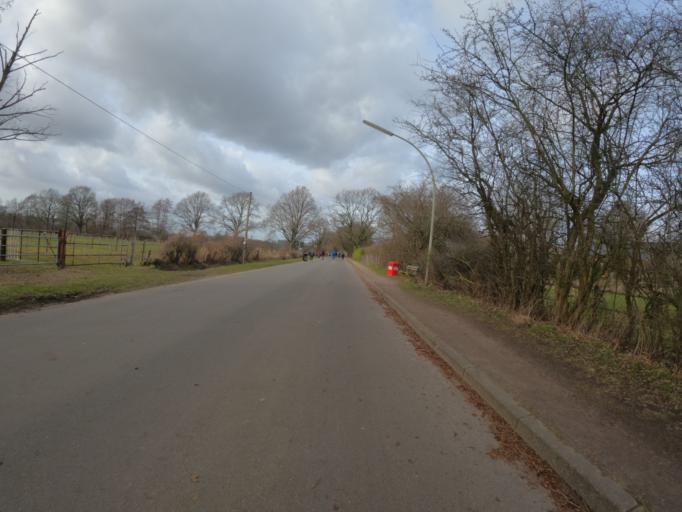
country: DE
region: Schleswig-Holstein
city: Halstenbek
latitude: 53.5826
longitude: 9.8398
